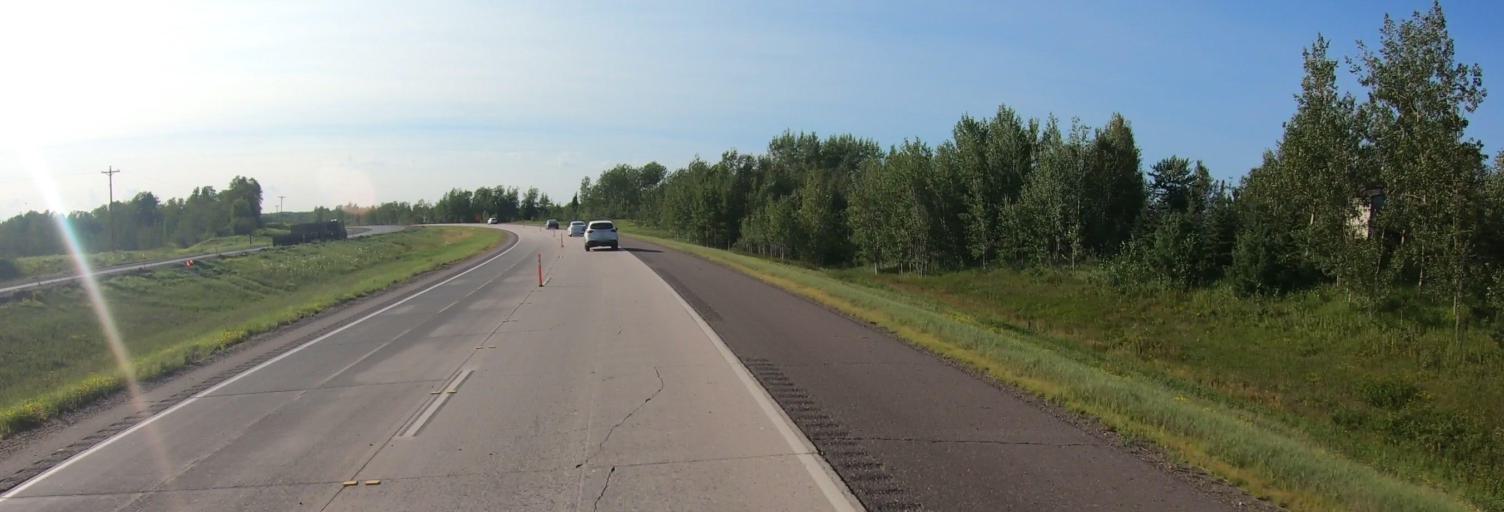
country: US
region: Minnesota
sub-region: Saint Louis County
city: Hermantown
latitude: 46.9201
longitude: -92.4015
